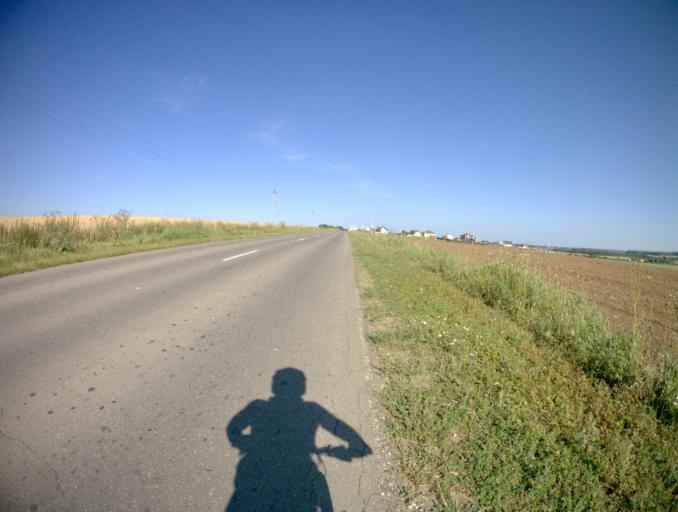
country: RU
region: Vladimir
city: Bogolyubovo
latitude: 56.2932
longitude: 40.5488
